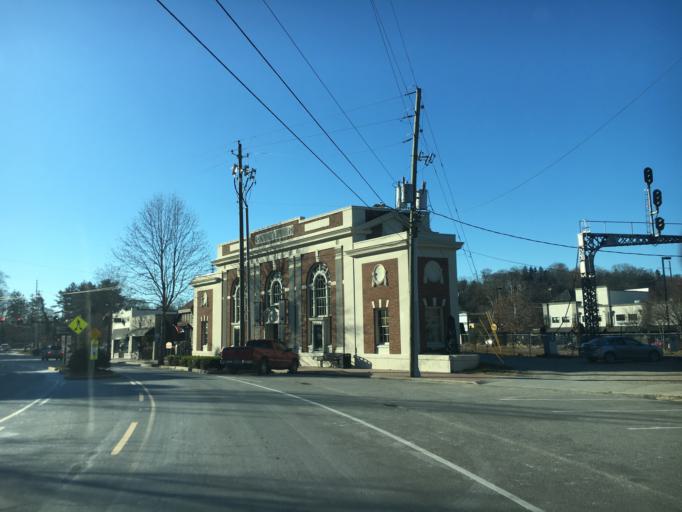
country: US
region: North Carolina
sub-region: Buncombe County
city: Asheville
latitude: 35.5675
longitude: -82.5425
